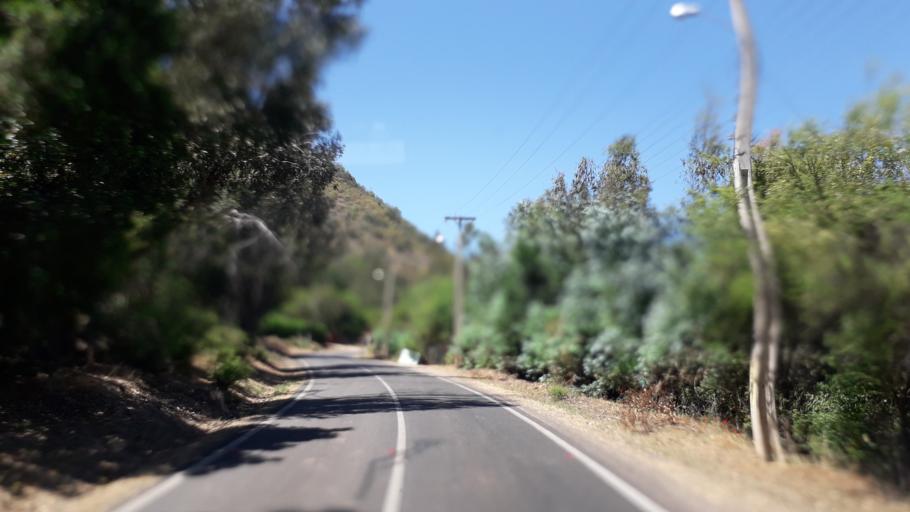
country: CL
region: Valparaiso
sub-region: Provincia de Marga Marga
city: Limache
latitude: -33.0780
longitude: -71.2114
